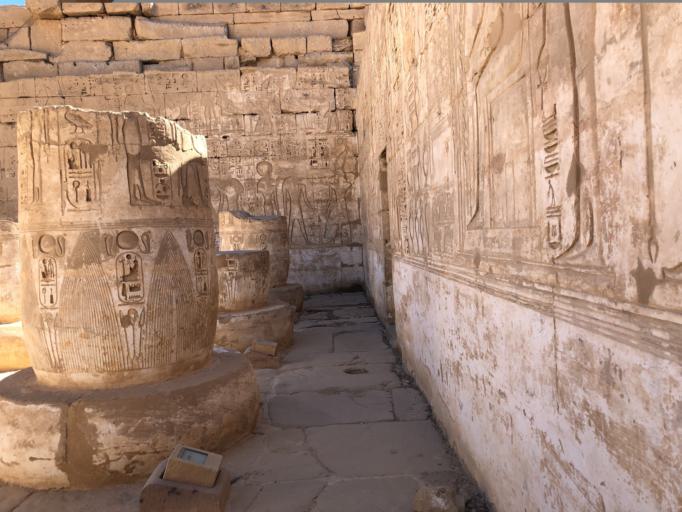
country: EG
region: Luxor
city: Luxor
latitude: 25.7199
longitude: 32.6004
